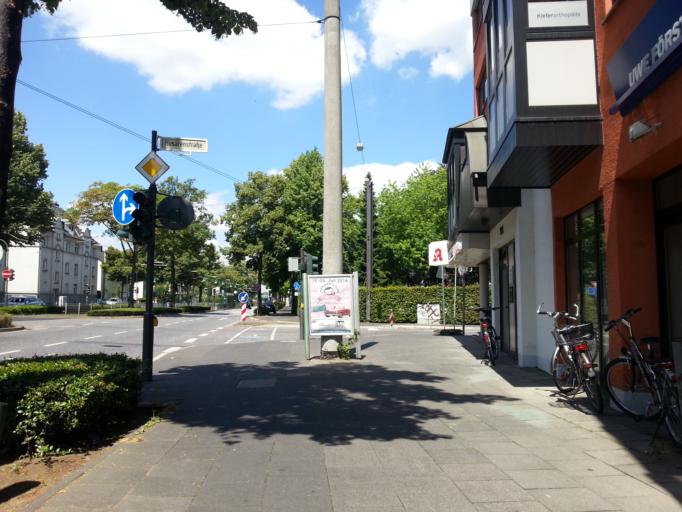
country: DE
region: North Rhine-Westphalia
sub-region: Regierungsbezirk Koln
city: Bonn
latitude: 50.7476
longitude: 7.0942
